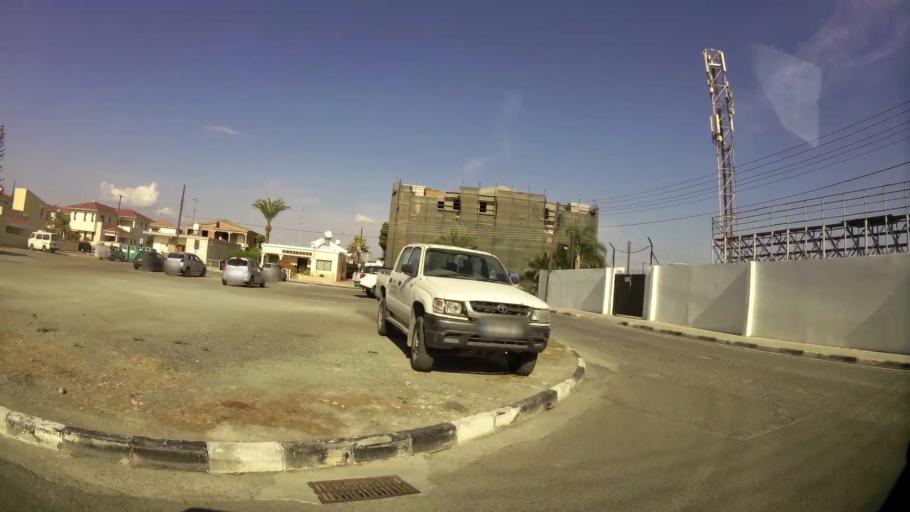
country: CY
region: Larnaka
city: Aradippou
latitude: 34.9482
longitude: 33.5873
